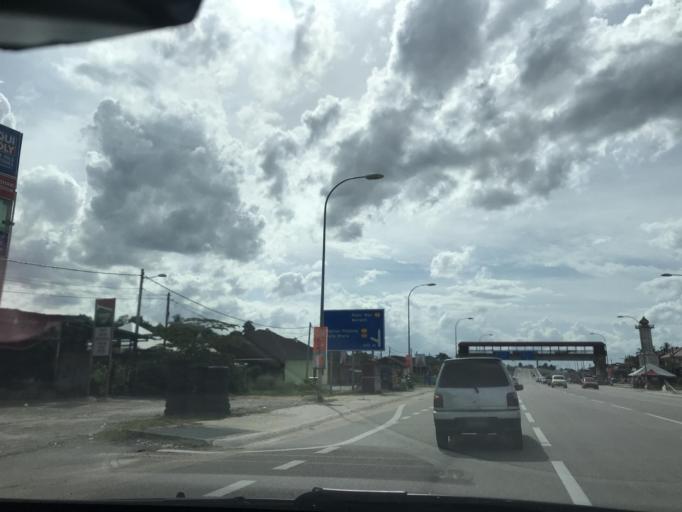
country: MY
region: Kelantan
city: Kampung Lemal
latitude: 6.0259
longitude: 102.1458
